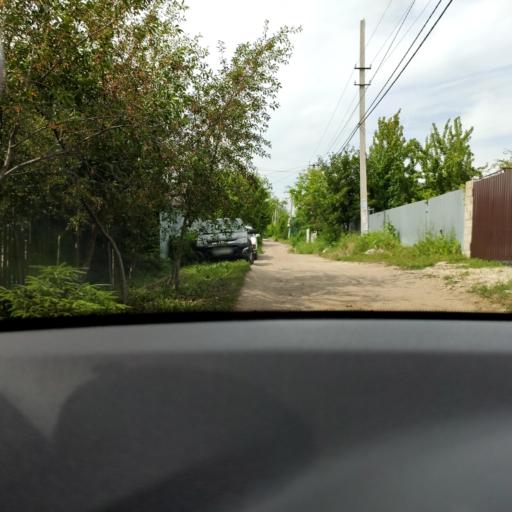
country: RU
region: Samara
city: Petra-Dubrava
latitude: 53.2834
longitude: 50.2871
